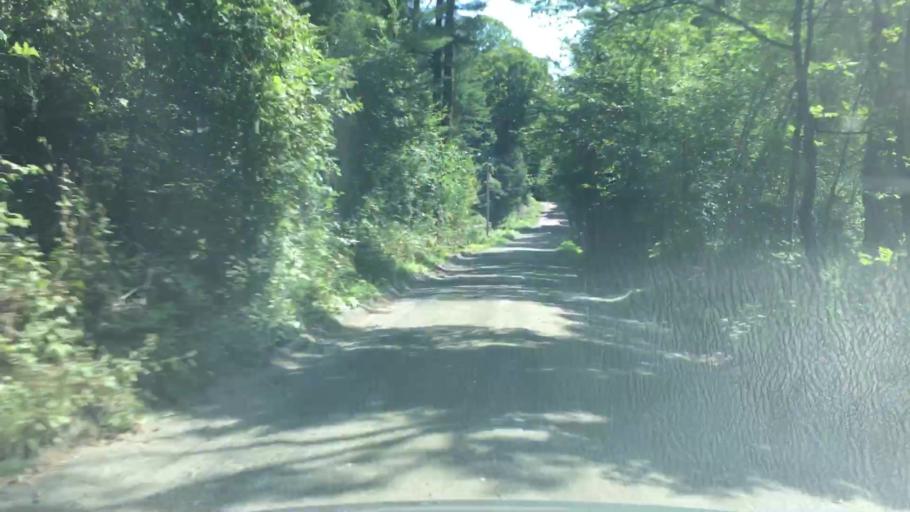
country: US
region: Vermont
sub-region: Windham County
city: West Brattleboro
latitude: 42.7987
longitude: -72.6396
